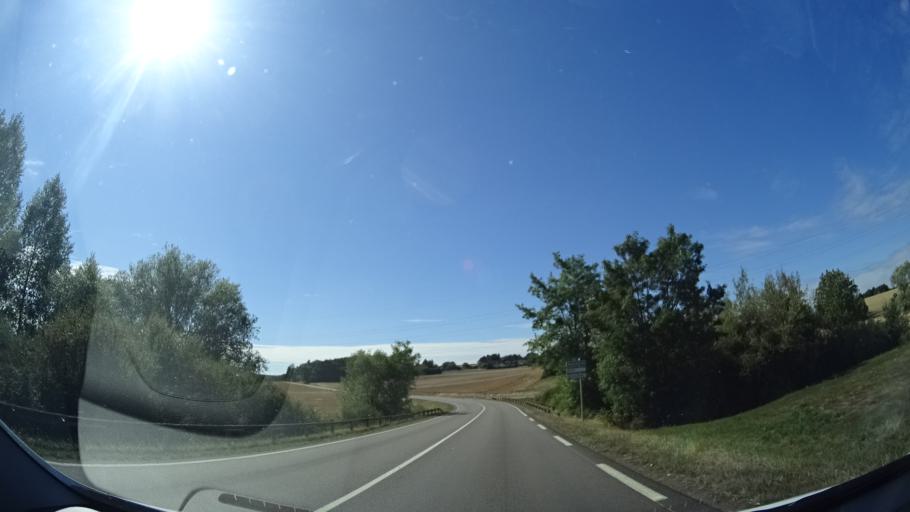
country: FR
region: Bourgogne
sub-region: Departement de l'Yonne
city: Charny
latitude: 47.9379
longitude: 3.1244
